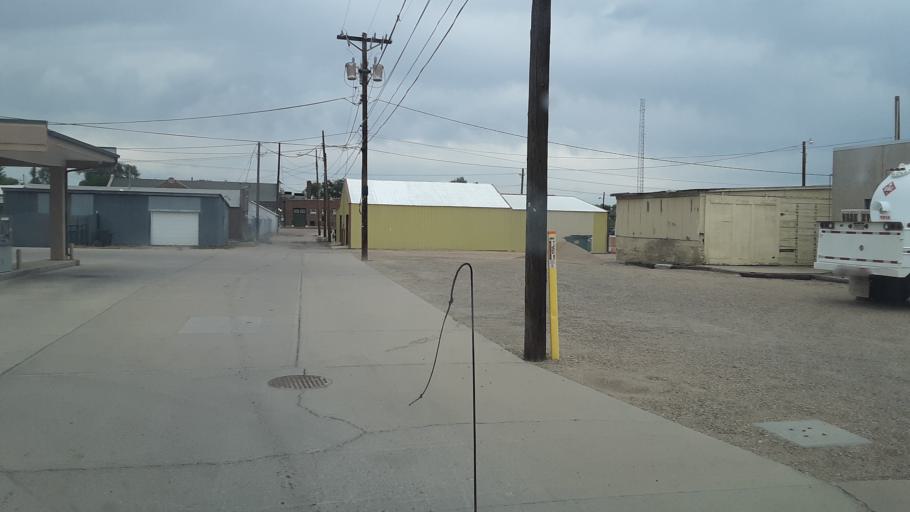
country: US
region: Colorado
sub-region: Otero County
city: Fowler
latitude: 38.1307
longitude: -104.0231
